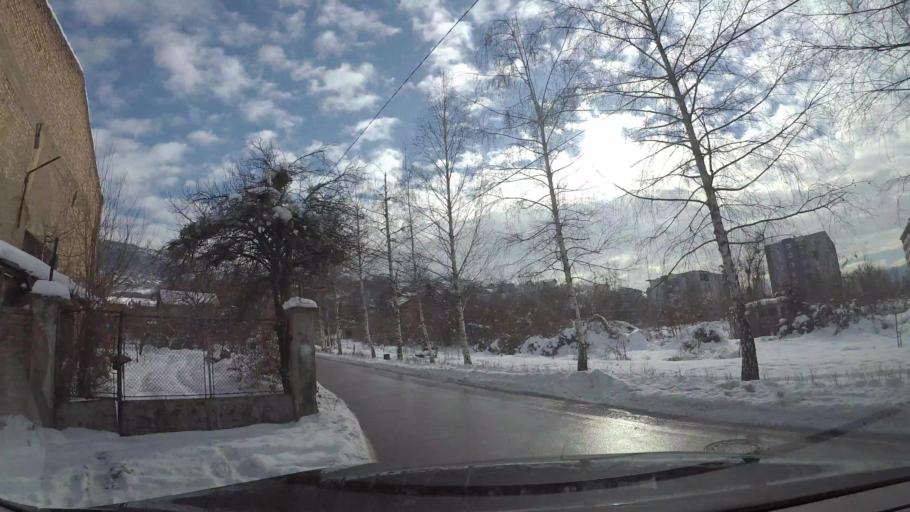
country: BA
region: Federation of Bosnia and Herzegovina
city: Kobilja Glava
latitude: 43.8819
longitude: 18.4153
